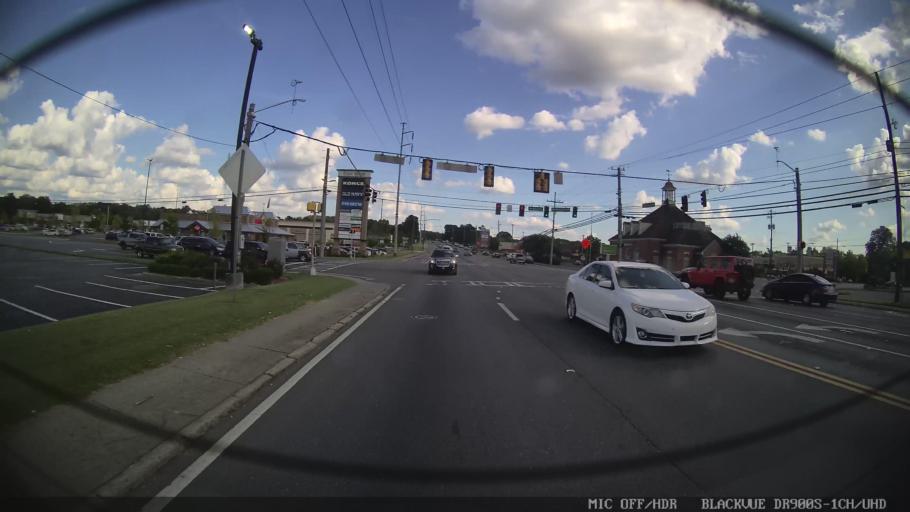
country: US
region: Georgia
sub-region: Floyd County
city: Rome
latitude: 34.2526
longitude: -85.1634
